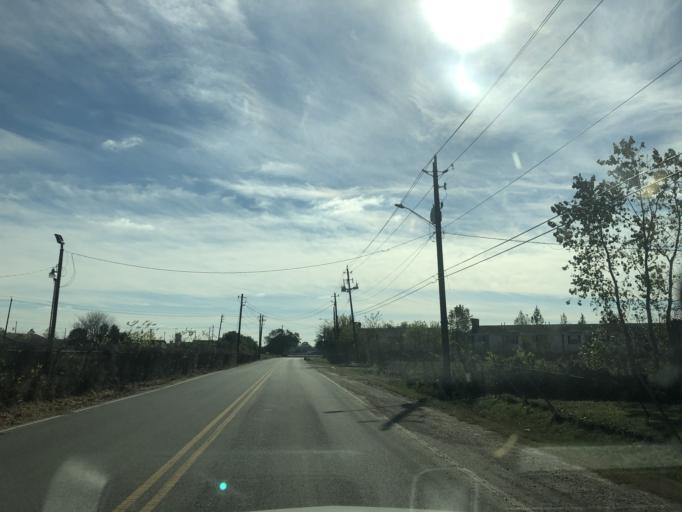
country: US
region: Texas
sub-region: Harris County
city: South Houston
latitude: 29.6578
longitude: -95.2506
